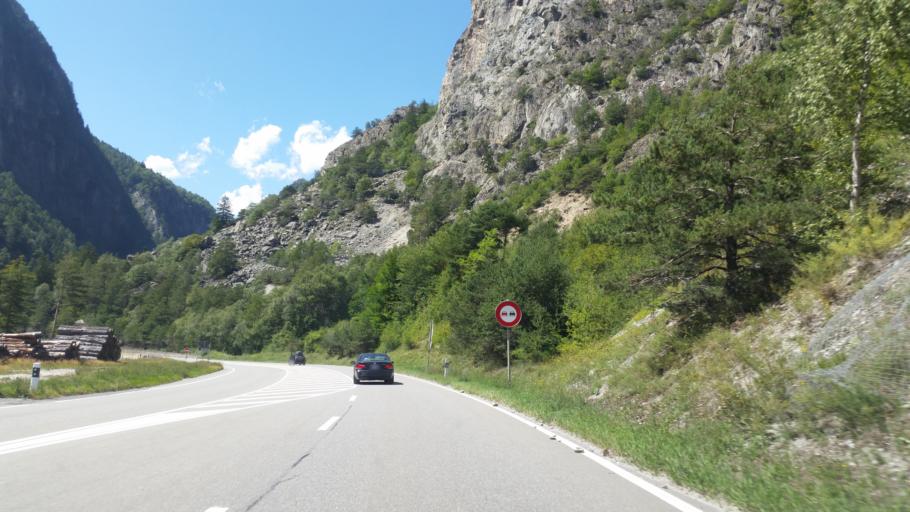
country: CH
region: Valais
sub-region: Martigny District
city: Charrat-les-Chenes
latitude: 46.0794
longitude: 7.1303
